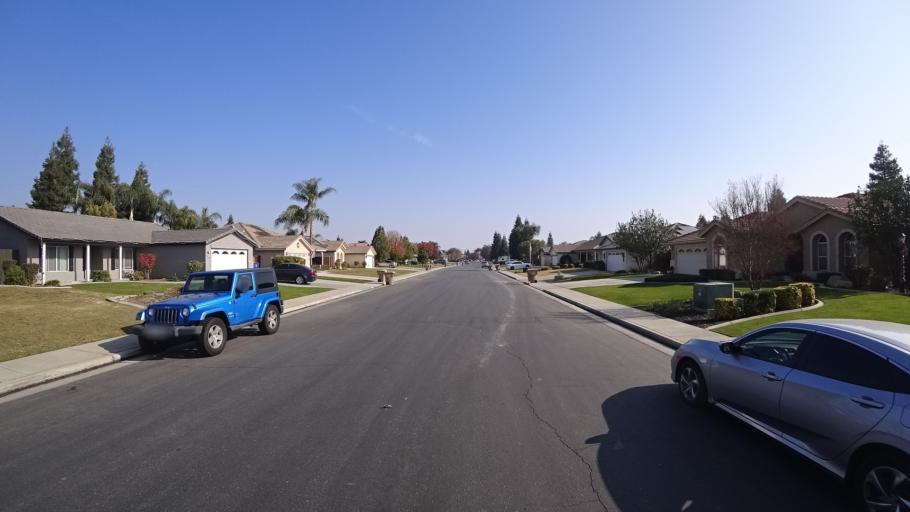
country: US
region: California
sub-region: Kern County
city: Greenacres
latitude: 35.4239
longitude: -119.1146
